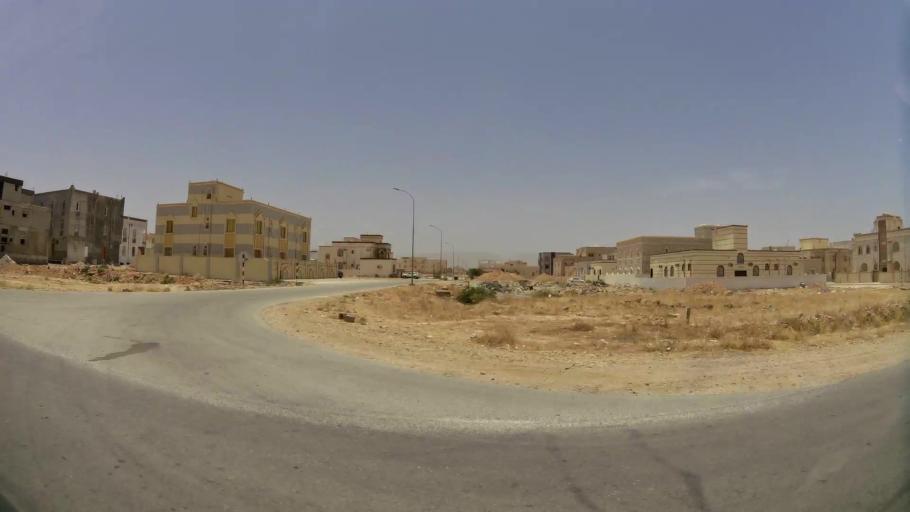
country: OM
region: Zufar
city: Salalah
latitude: 17.0895
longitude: 54.1571
